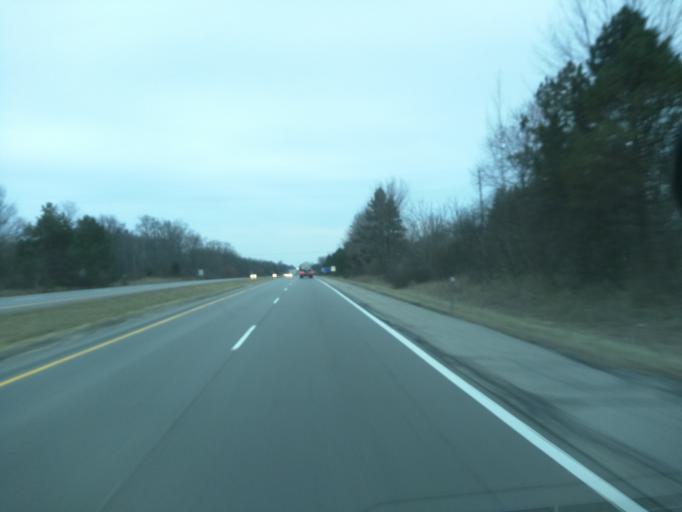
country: US
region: Michigan
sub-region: Ingham County
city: Leslie
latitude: 42.3946
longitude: -84.4293
